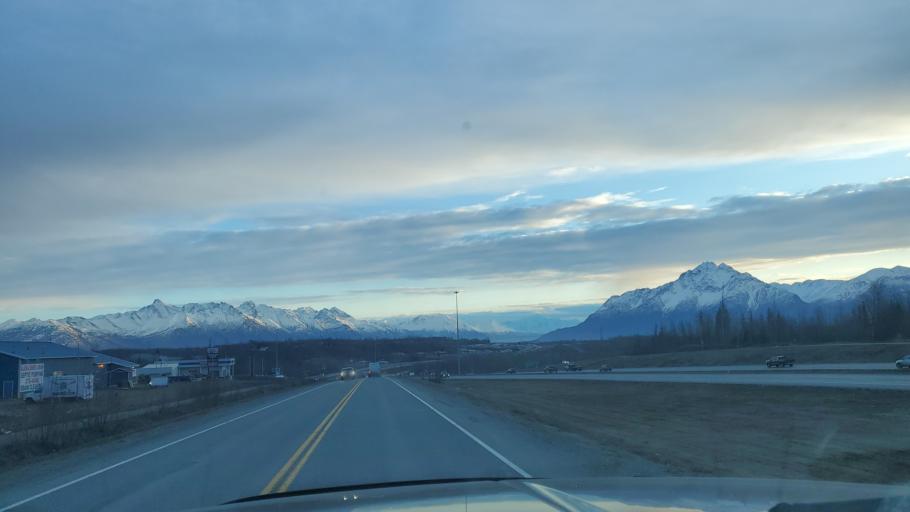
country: US
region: Alaska
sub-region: Matanuska-Susitna Borough
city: Lakes
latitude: 61.5692
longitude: -149.3334
